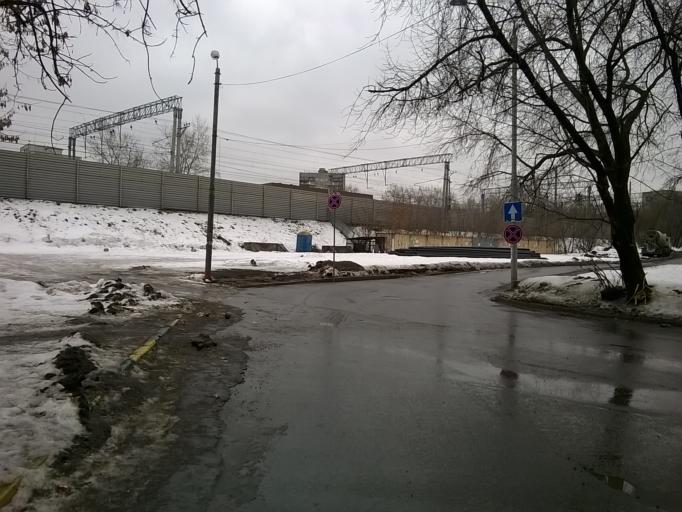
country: RU
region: Moscow
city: Lefortovo
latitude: 55.7787
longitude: 37.7093
